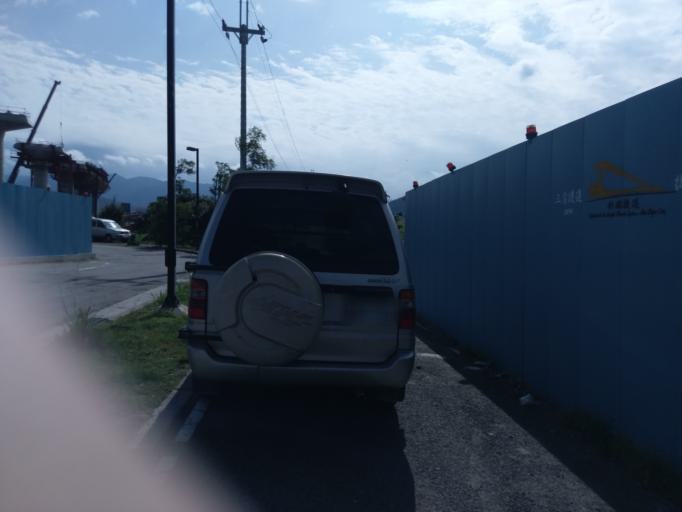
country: TW
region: Taiwan
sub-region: Taoyuan
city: Taoyuan
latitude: 24.9543
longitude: 121.3589
